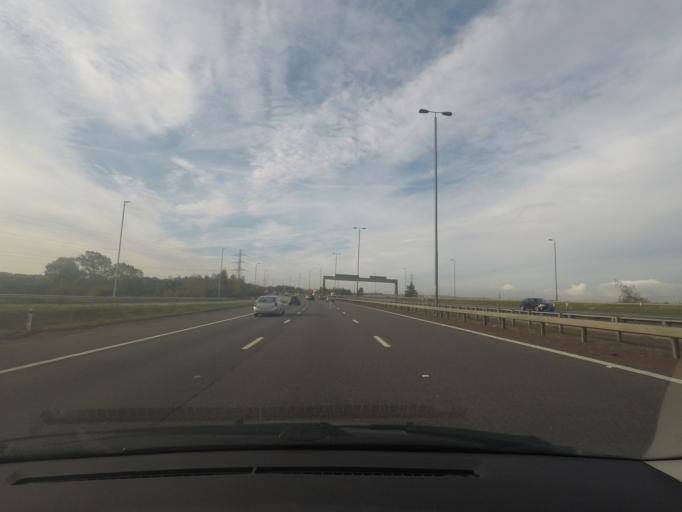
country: GB
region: England
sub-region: City and Borough of Leeds
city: Lofthouse
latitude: 53.7742
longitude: -1.4751
